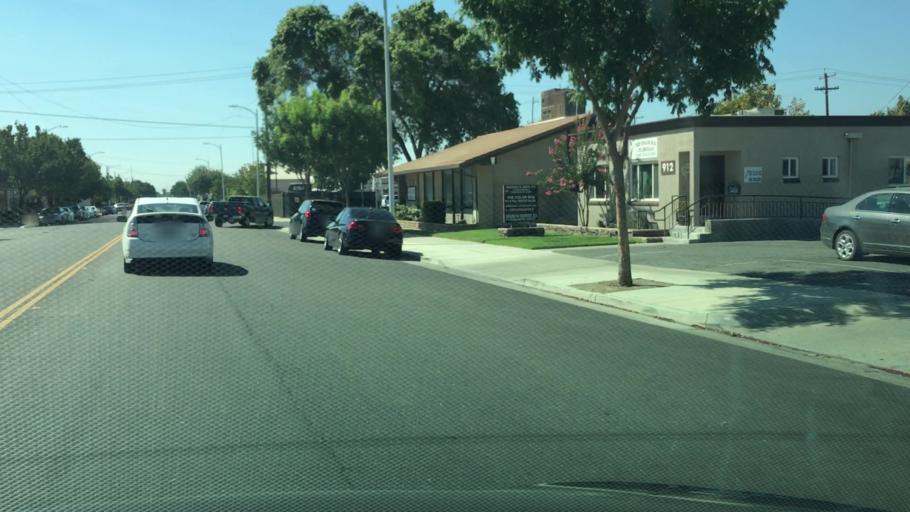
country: US
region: California
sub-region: Merced County
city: Los Banos
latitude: 37.0587
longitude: -120.8430
